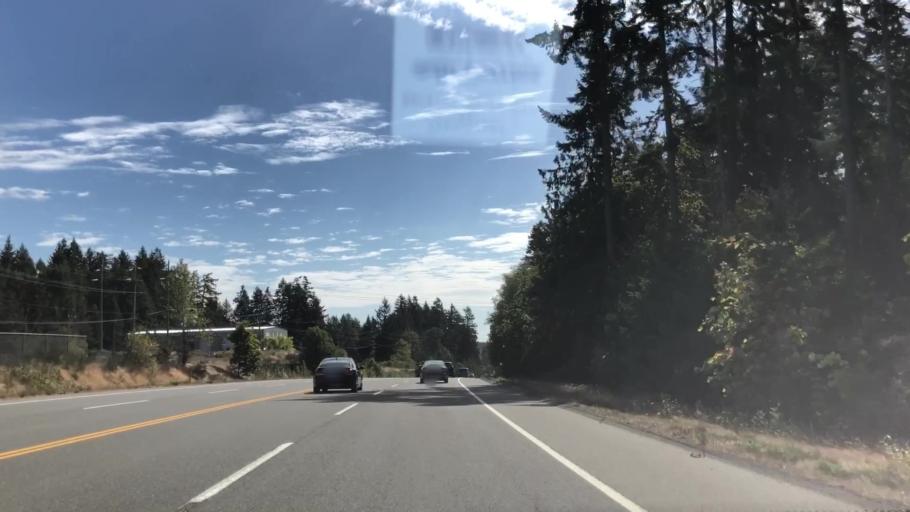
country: CA
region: British Columbia
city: Nanaimo
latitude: 49.1336
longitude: -123.8694
